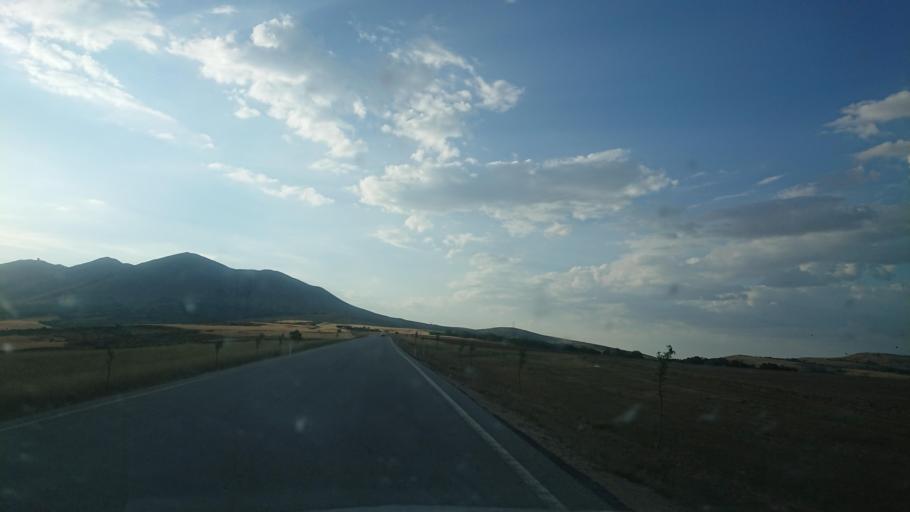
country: TR
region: Aksaray
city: Balci
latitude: 38.6142
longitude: 34.1006
